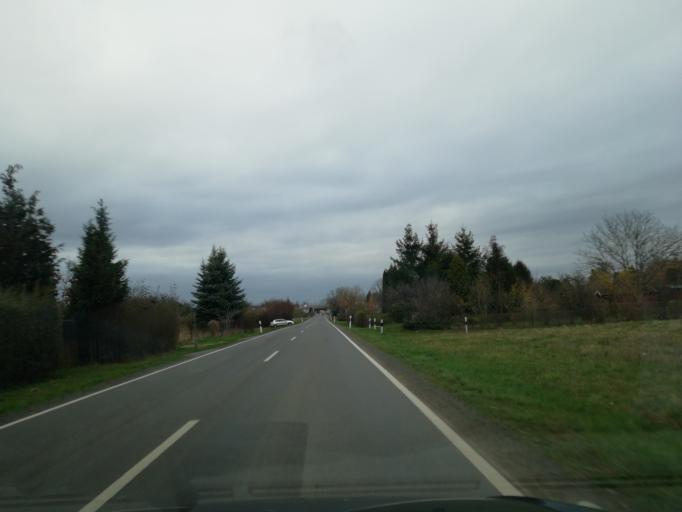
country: DE
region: Brandenburg
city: Vetschau
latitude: 51.7754
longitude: 14.0702
